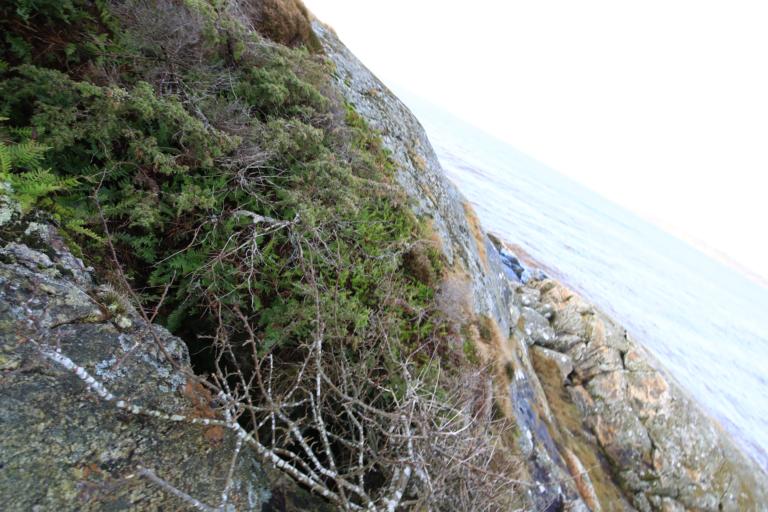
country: SE
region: Halland
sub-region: Kungsbacka Kommun
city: Frillesas
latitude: 57.2003
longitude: 12.1672
